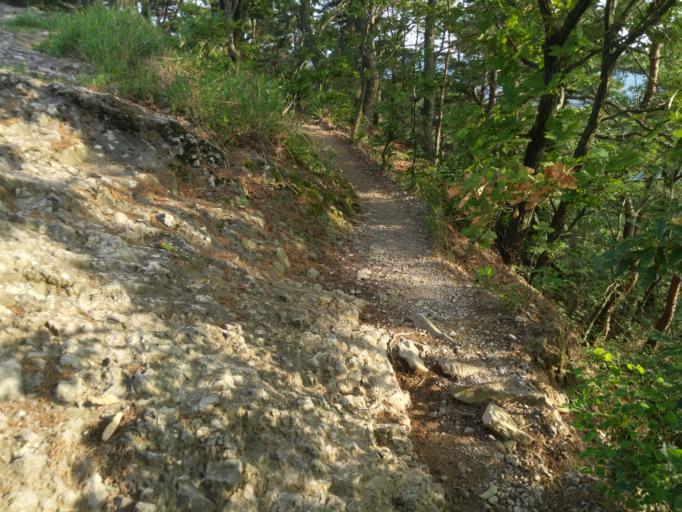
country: KR
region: Daegu
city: Hwawon
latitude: 35.7842
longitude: 128.5462
